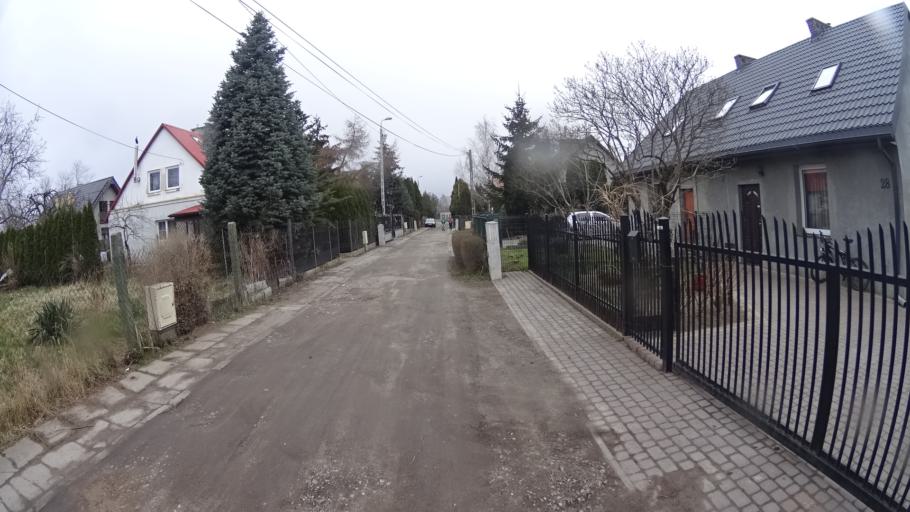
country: PL
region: Masovian Voivodeship
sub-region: Powiat warszawski zachodni
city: Blonie
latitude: 52.2170
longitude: 20.6481
